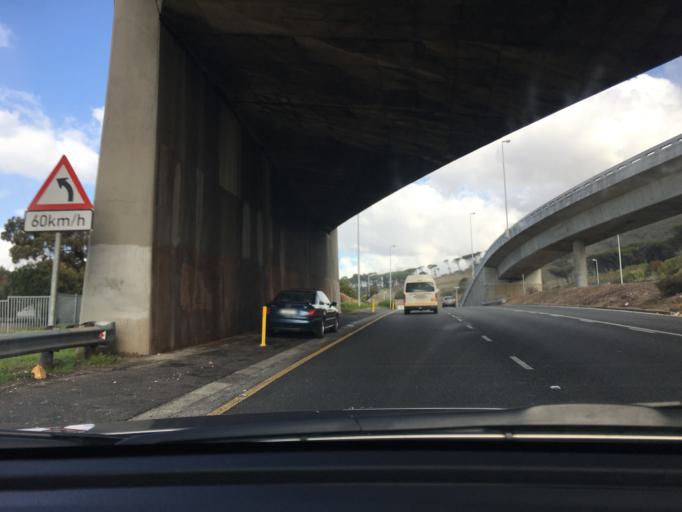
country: ZA
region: Western Cape
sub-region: City of Cape Town
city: Rosebank
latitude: -33.9403
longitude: 18.4579
